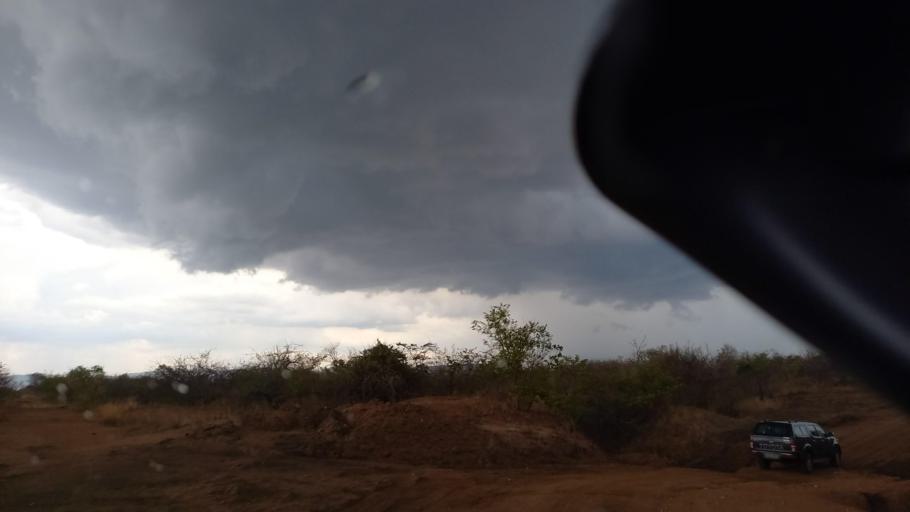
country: ZM
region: Lusaka
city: Kafue
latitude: -15.8678
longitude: 28.1906
